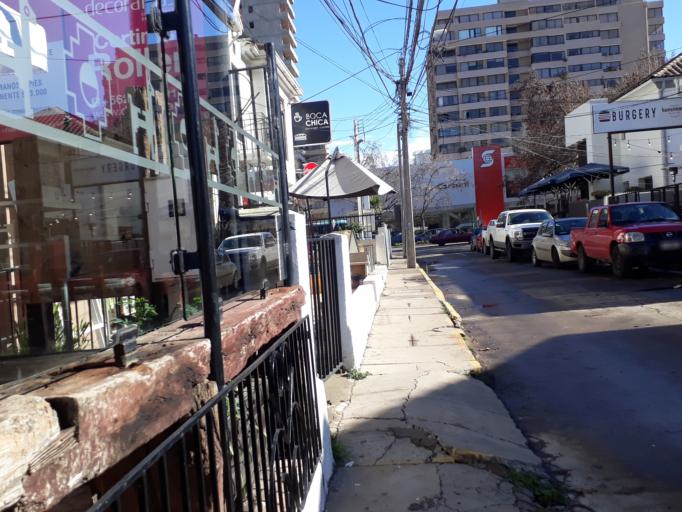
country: CL
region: Valparaiso
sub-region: Provincia de Valparaiso
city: Vina del Mar
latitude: -33.0129
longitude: -71.5487
